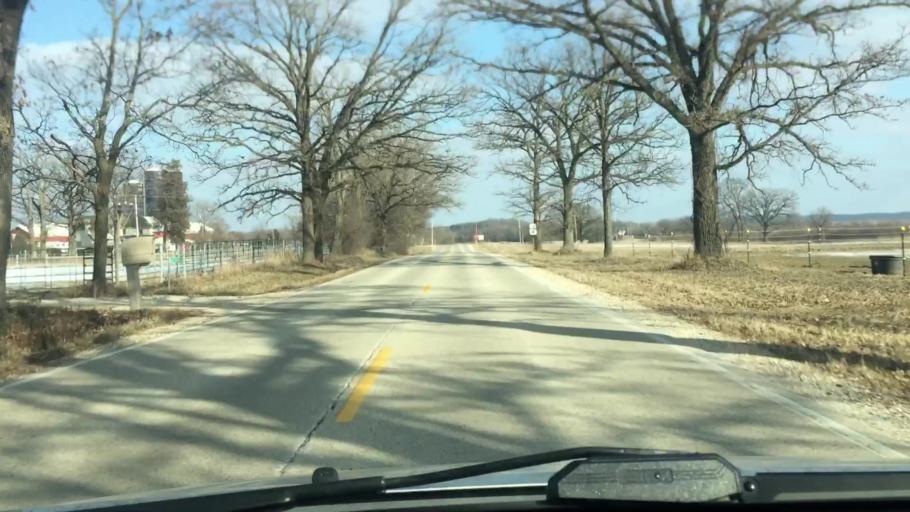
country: US
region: Wisconsin
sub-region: Waukesha County
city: Eagle
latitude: 42.9160
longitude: -88.5226
